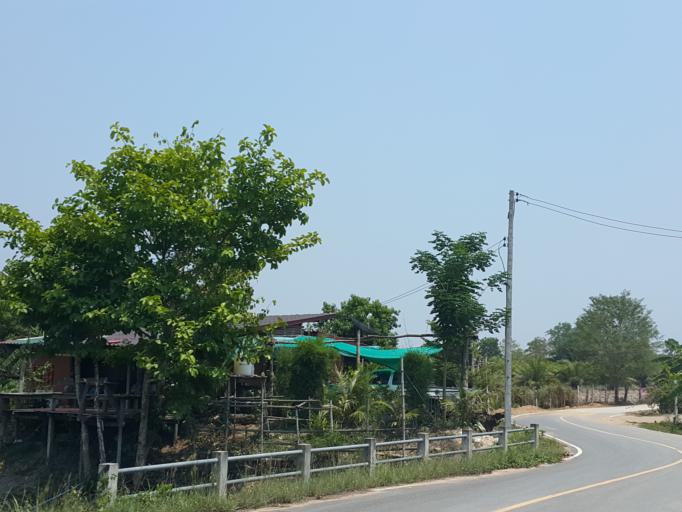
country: TH
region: Kanchanaburi
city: Sai Yok
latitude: 14.1730
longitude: 98.9582
